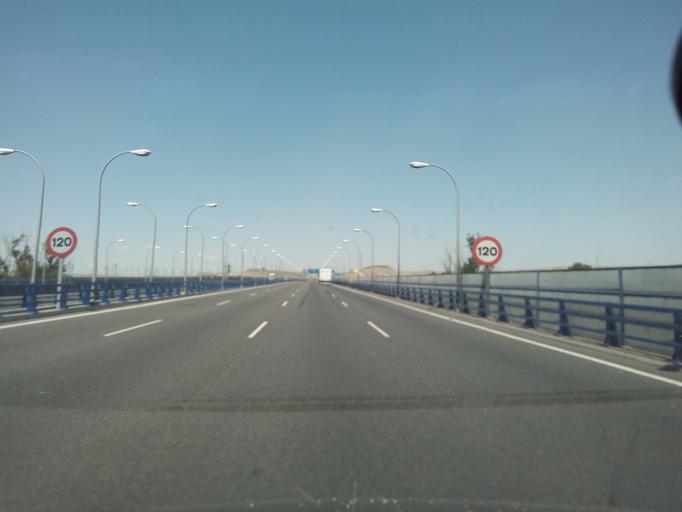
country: ES
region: Madrid
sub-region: Provincia de Madrid
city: Villa de Vallecas
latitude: 40.3235
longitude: -3.6426
